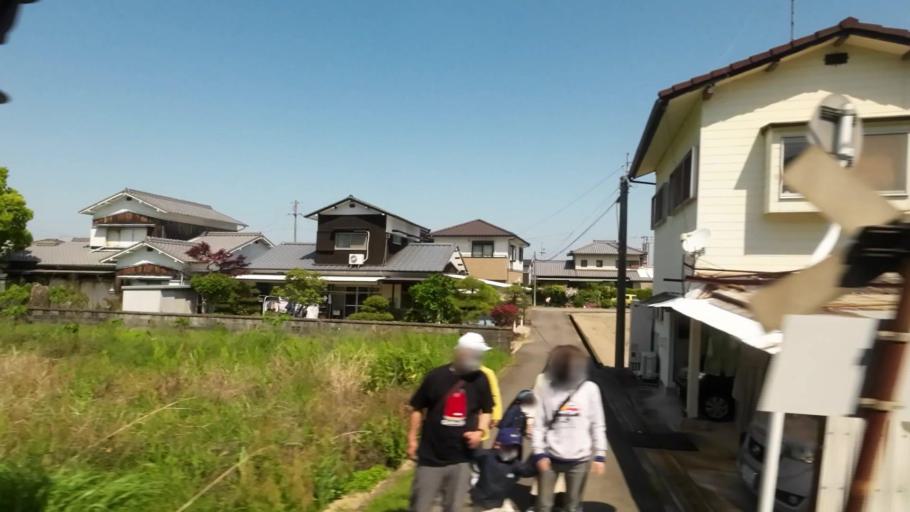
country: JP
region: Ehime
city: Niihama
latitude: 33.9626
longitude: 133.3122
